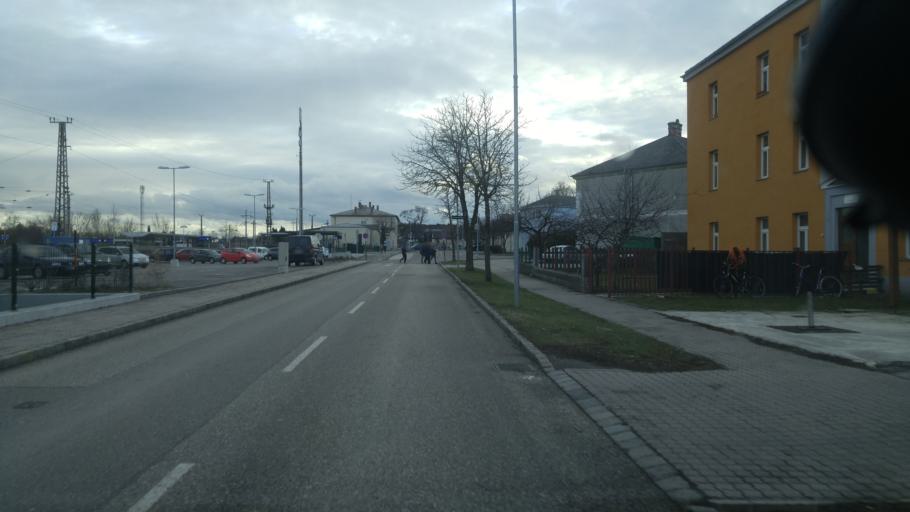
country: AT
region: Lower Austria
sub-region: Politischer Bezirk Baden
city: Bad Voslau
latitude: 47.9707
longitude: 16.2231
